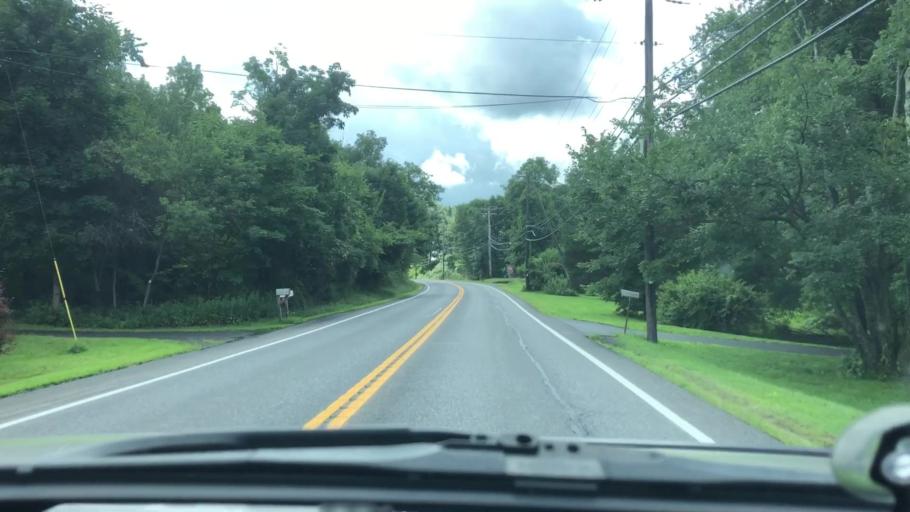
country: US
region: New York
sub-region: Ulster County
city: Manorville
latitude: 42.1304
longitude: -73.9981
